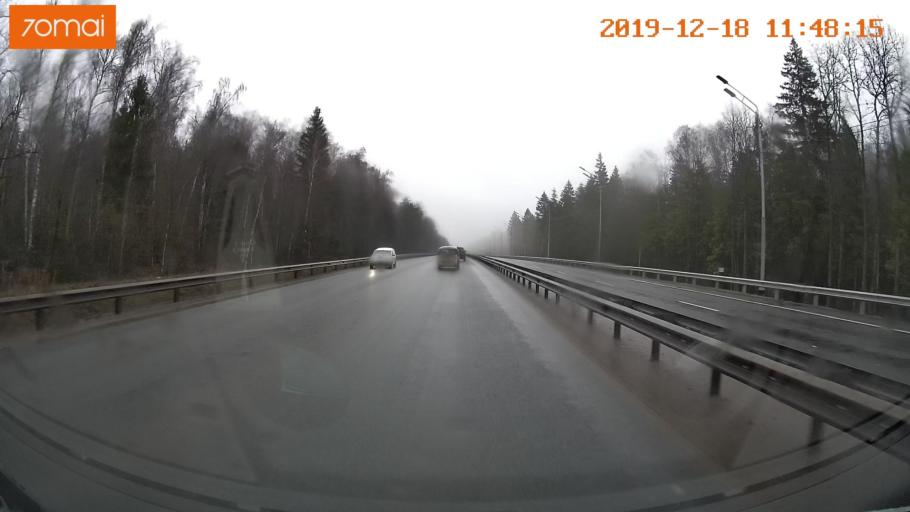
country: RU
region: Moskovskaya
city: Yershovo
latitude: 55.7661
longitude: 36.9019
